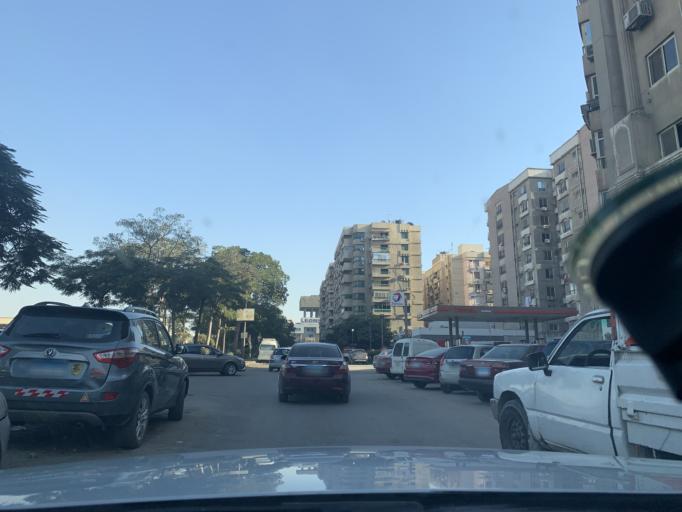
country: EG
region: Muhafazat al Qahirah
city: Cairo
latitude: 30.0377
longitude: 31.3464
